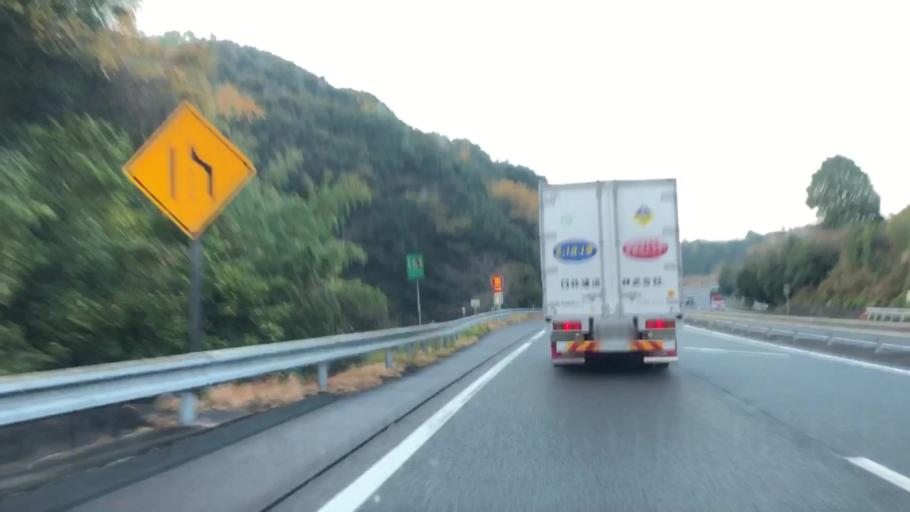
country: JP
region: Nagasaki
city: Sasebo
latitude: 33.1552
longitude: 129.8127
